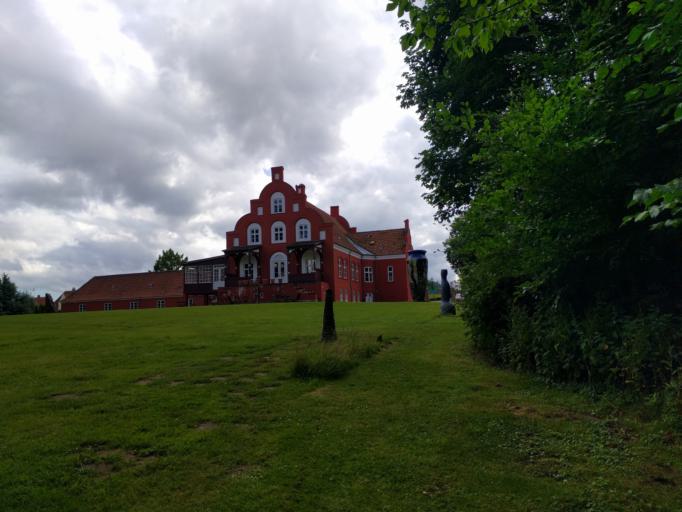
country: DK
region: South Denmark
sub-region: Middelfart Kommune
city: Middelfart
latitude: 55.5084
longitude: 9.7202
